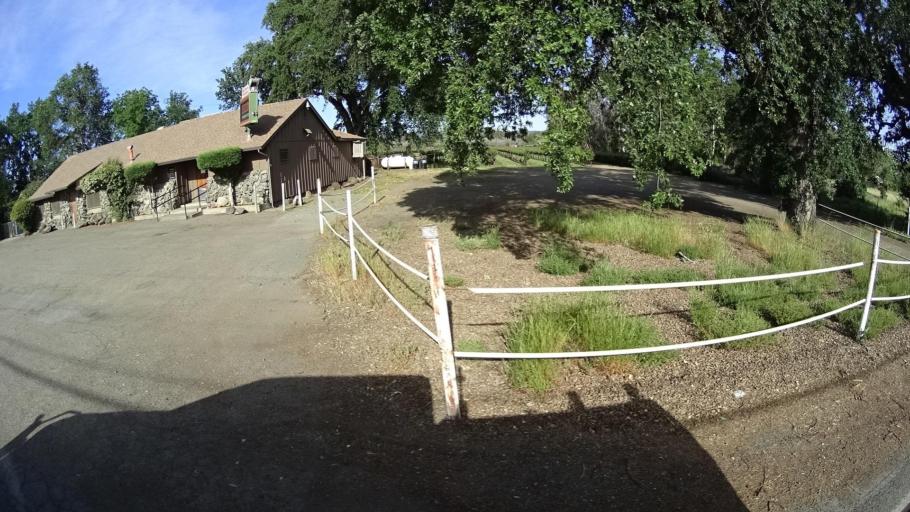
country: US
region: California
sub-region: Lake County
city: Kelseyville
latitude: 39.0027
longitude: -122.8756
